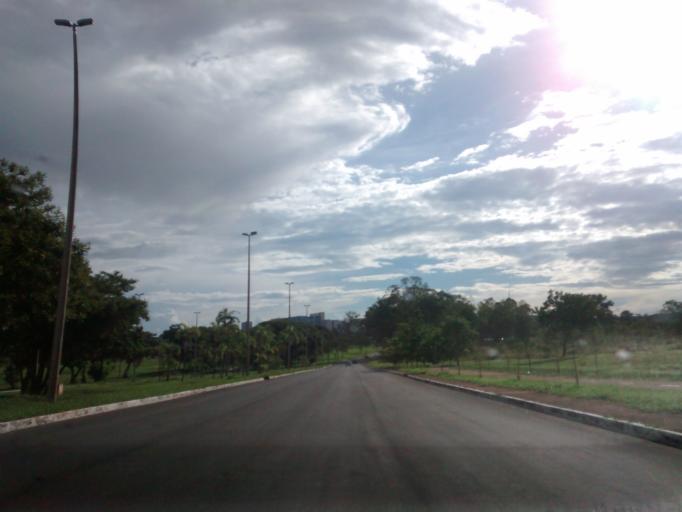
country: BR
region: Federal District
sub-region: Brasilia
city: Brasilia
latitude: -15.7768
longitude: -47.8662
